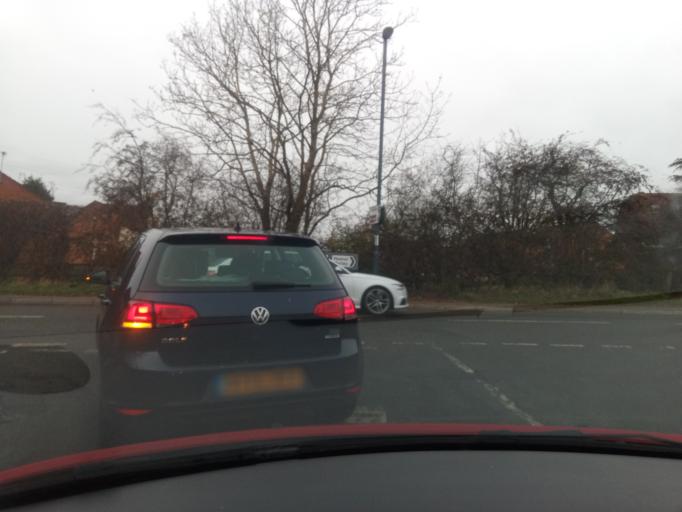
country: GB
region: England
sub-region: Derbyshire
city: Borrowash
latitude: 52.9483
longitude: -1.4122
